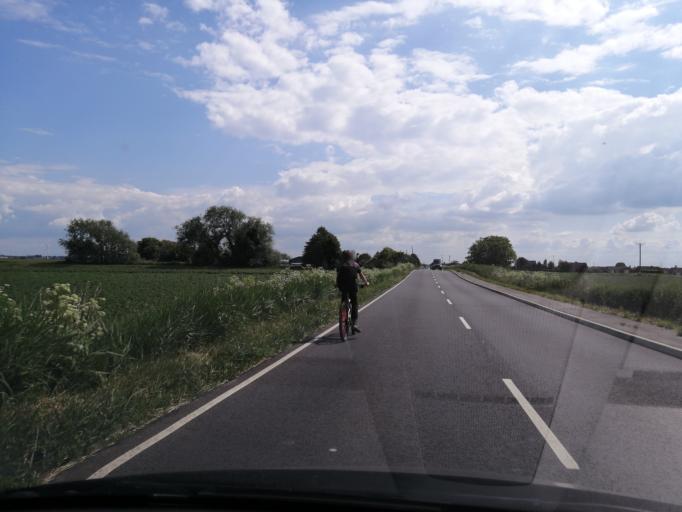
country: GB
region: England
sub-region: Cambridgeshire
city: Ramsey
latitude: 52.4922
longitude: -0.1482
